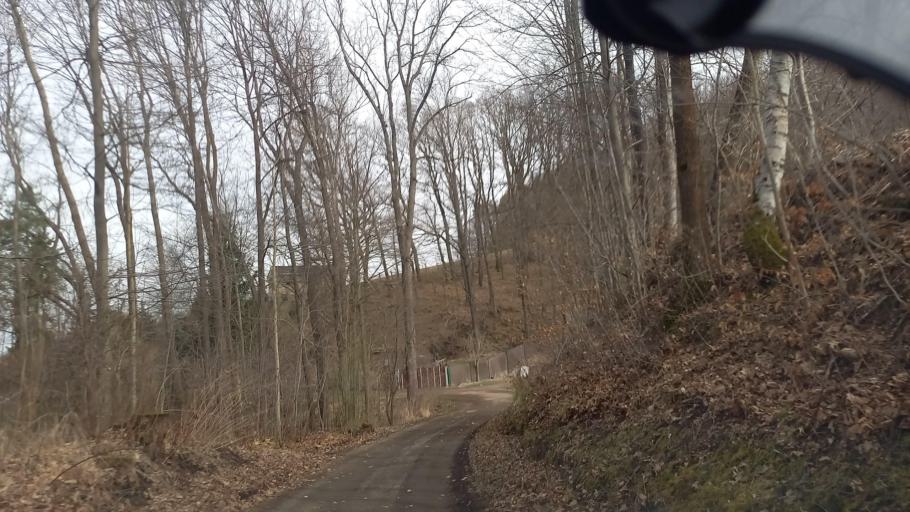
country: DE
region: Saxony
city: Kirchberg
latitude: 50.6342
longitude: 12.5230
